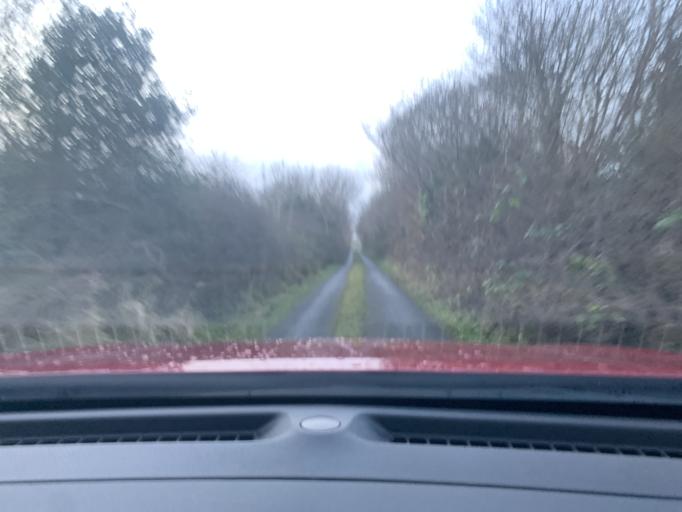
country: IE
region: Connaught
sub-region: Sligo
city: Ballymote
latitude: 53.9902
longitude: -8.4484
